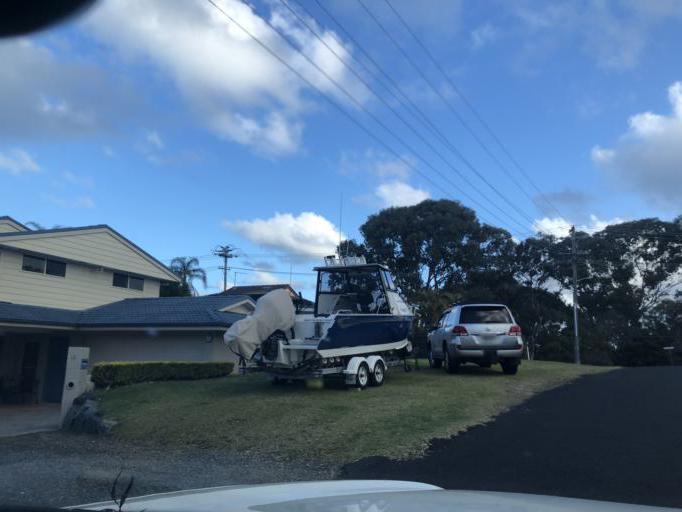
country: AU
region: New South Wales
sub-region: Coffs Harbour
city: Woolgoolga
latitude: -30.0964
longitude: 153.1967
